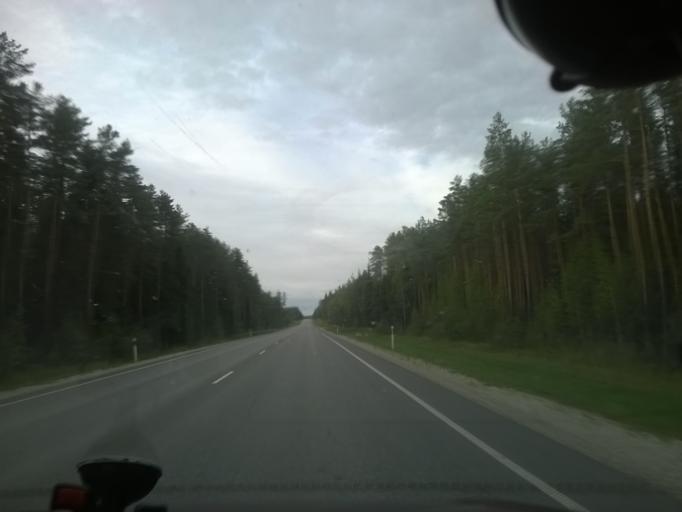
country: EE
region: Vorumaa
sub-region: Voru linn
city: Voru
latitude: 57.9419
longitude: 26.7964
